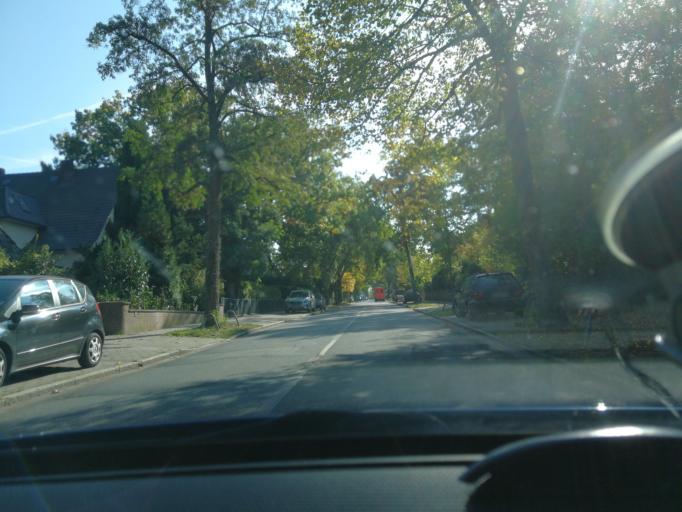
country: DE
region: Hamburg
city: Harburg
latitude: 53.4672
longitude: 9.9474
